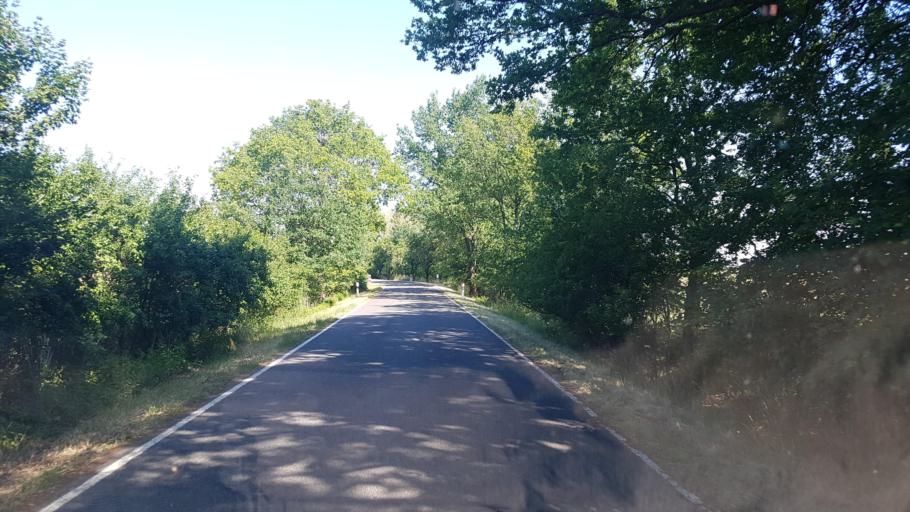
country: DE
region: Saxony-Anhalt
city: Elster
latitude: 51.7679
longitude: 12.8468
